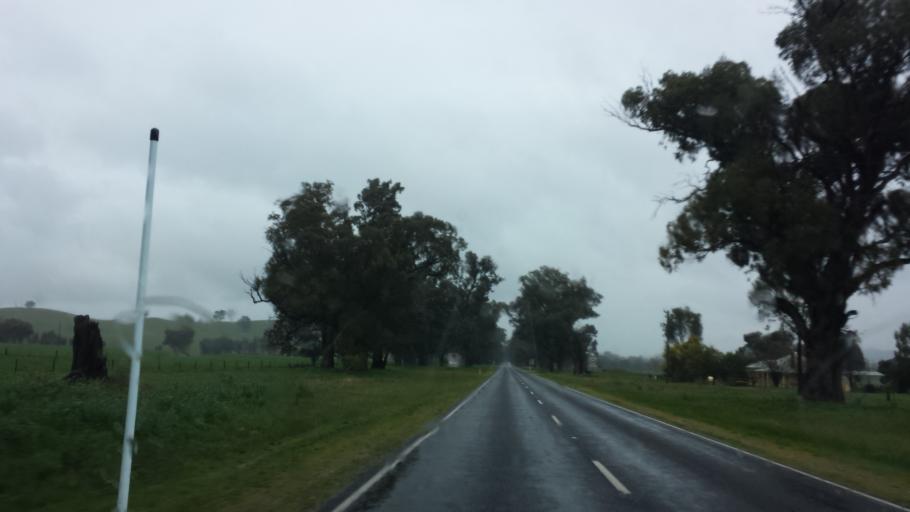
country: AU
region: Victoria
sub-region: Wangaratta
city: Wangaratta
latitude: -36.4383
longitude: 146.5457
